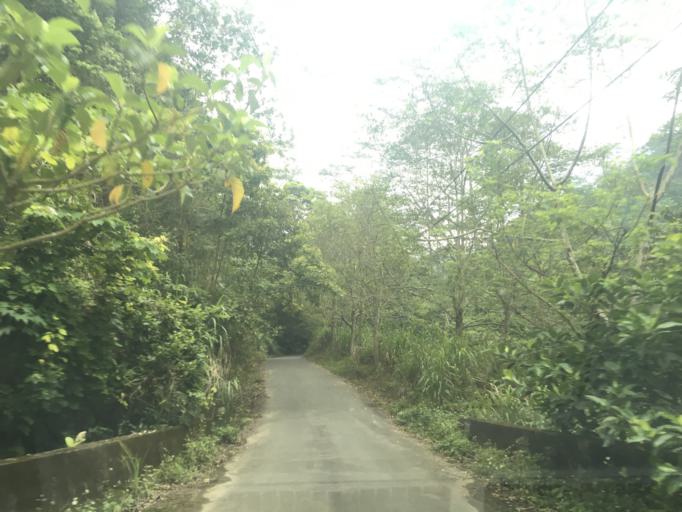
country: TW
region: Taiwan
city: Zhongxing New Village
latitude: 24.0477
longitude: 120.7860
